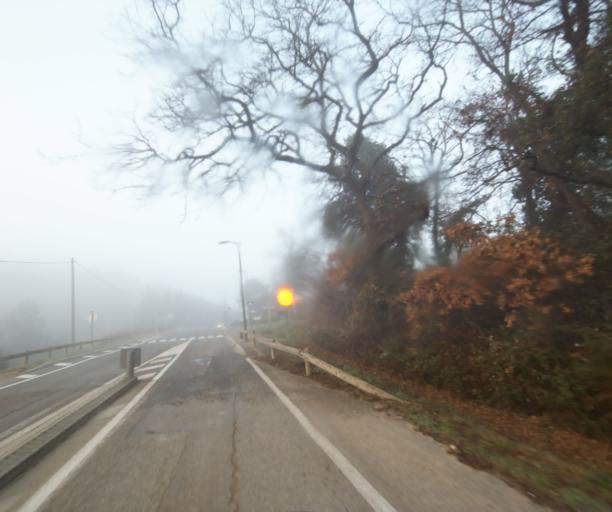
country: FR
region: Provence-Alpes-Cote d'Azur
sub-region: Departement des Bouches-du-Rhone
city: Meyreuil
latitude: 43.4828
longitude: 5.4980
